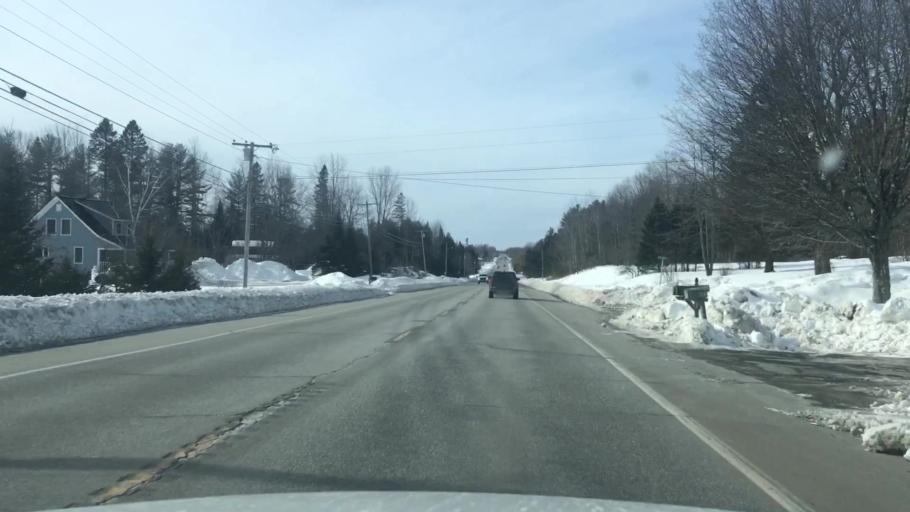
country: US
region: Maine
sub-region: Penobscot County
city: Kenduskeag
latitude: 44.9757
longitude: -68.9866
